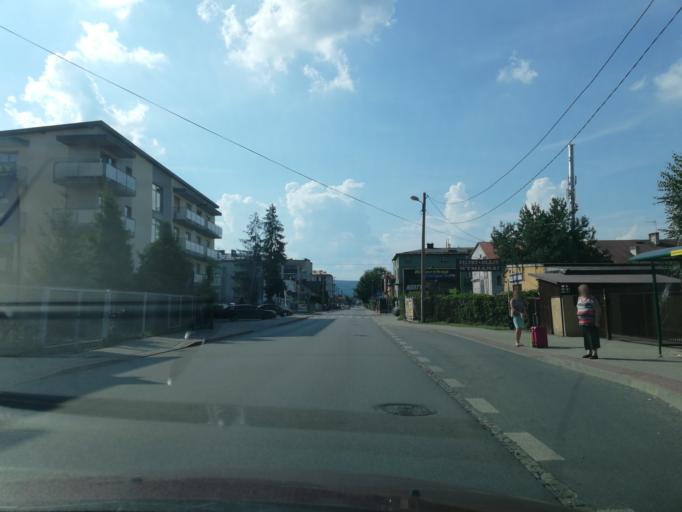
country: PL
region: Lesser Poland Voivodeship
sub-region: Powiat nowosadecki
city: Nowy Sacz
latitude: 49.6269
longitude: 20.7063
